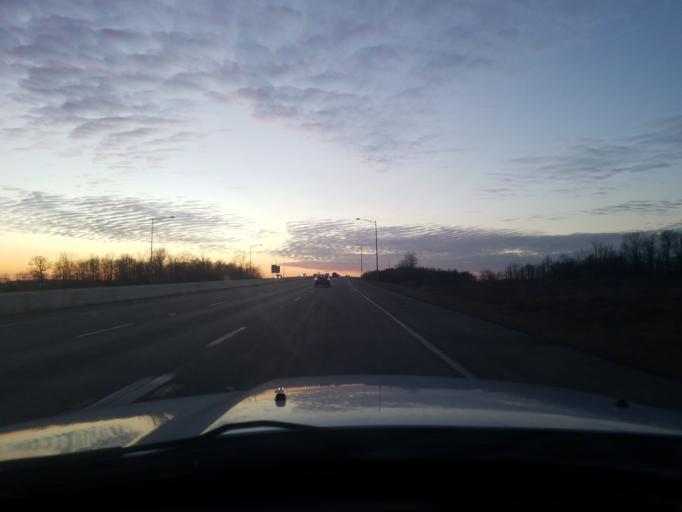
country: US
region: Indiana
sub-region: Wells County
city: Ossian
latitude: 40.9544
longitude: -85.1726
